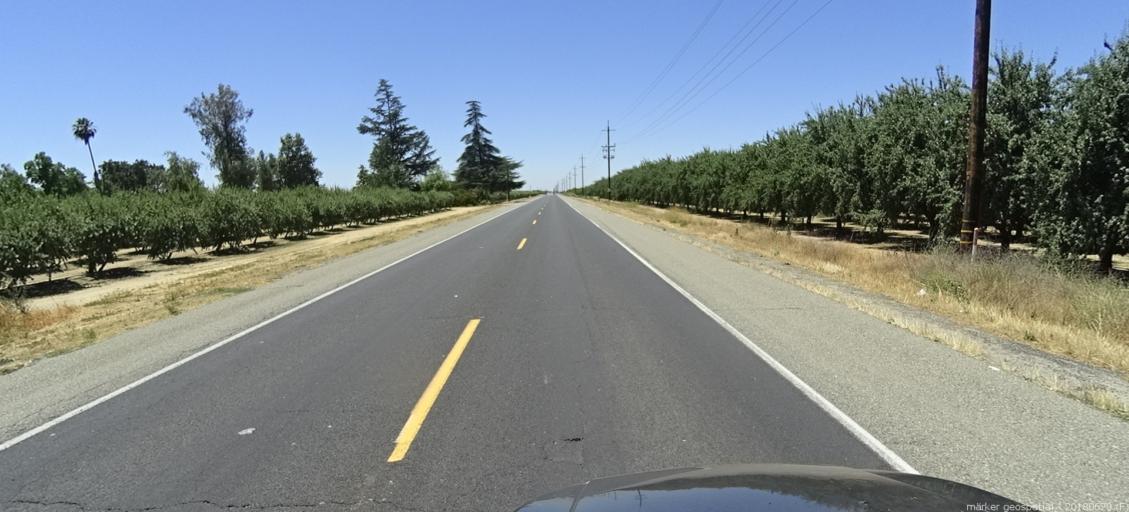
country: US
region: California
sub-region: Madera County
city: Parkwood
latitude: 36.9239
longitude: -120.0673
